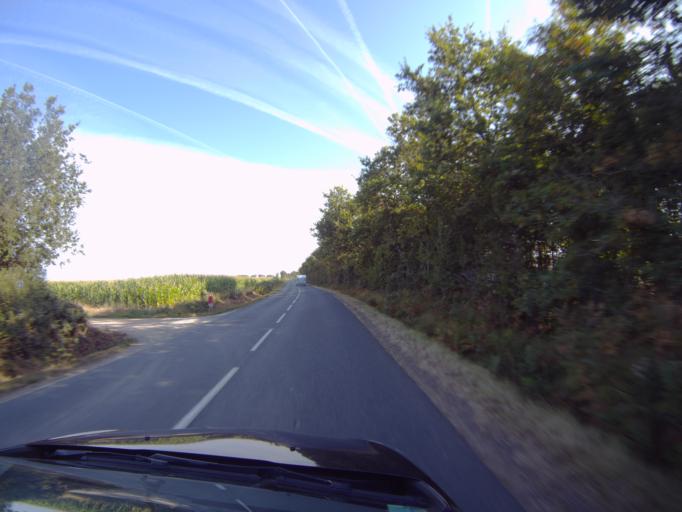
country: FR
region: Pays de la Loire
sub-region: Departement de la Vendee
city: Saint-Hilaire-de-Talmont
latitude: 46.4903
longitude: -1.5845
